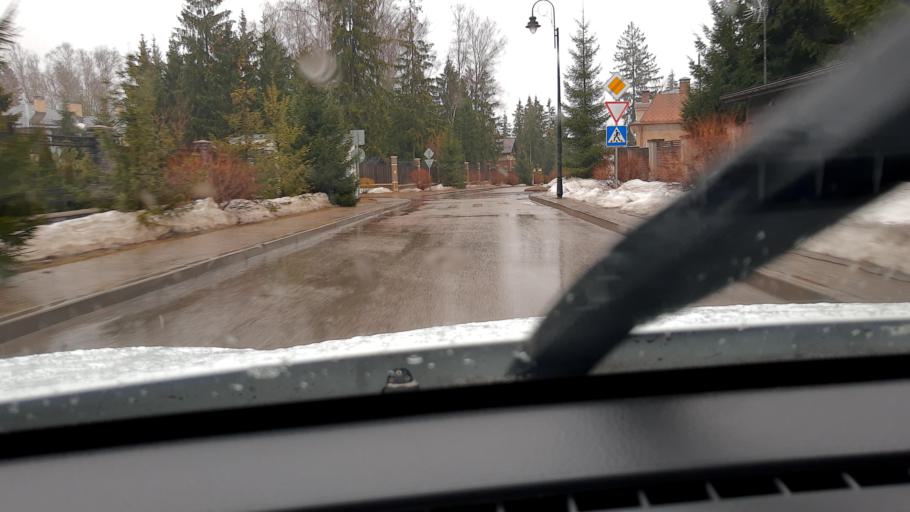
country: RU
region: Moskovskaya
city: Moskovskiy
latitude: 55.5801
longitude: 37.3964
